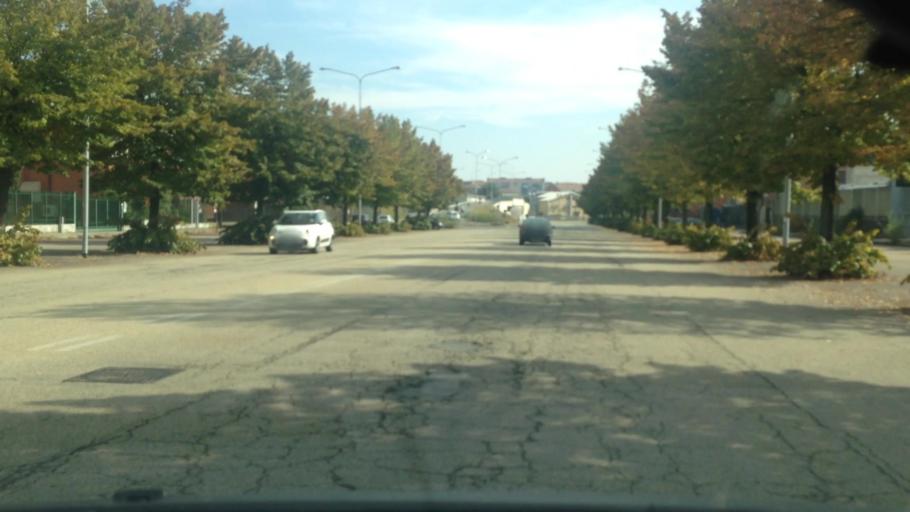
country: IT
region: Piedmont
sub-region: Provincia di Torino
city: Venaria Reale
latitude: 45.1171
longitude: 7.6447
